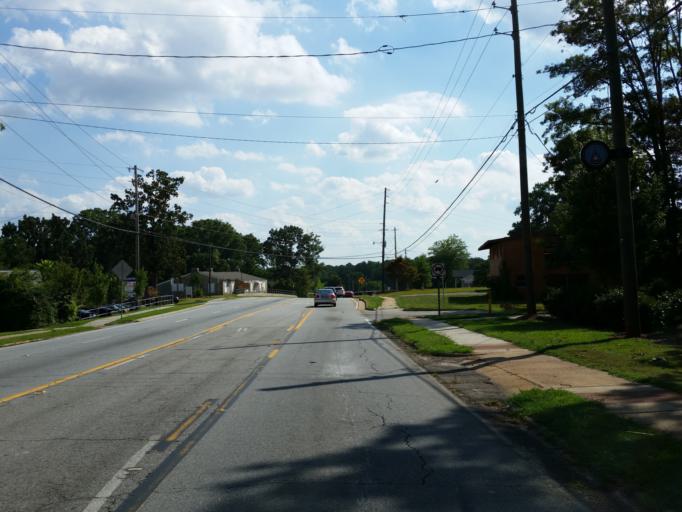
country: US
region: Georgia
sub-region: Gwinnett County
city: Lawrenceville
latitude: 33.9594
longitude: -83.9739
